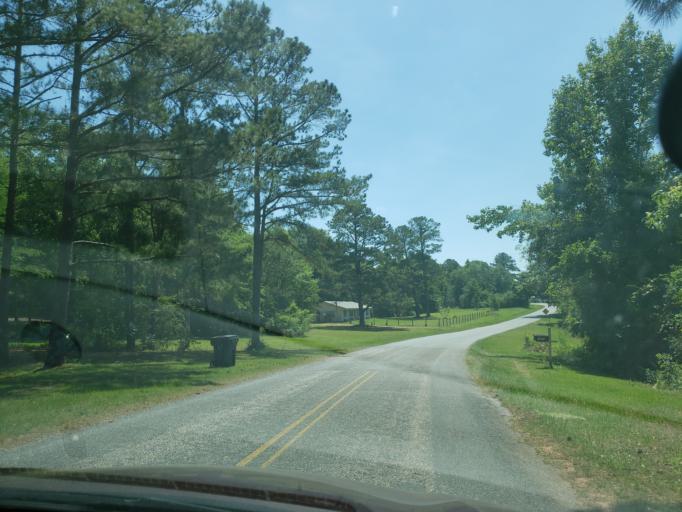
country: US
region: Alabama
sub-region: Elmore County
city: Tallassee
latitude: 32.5900
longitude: -85.8613
